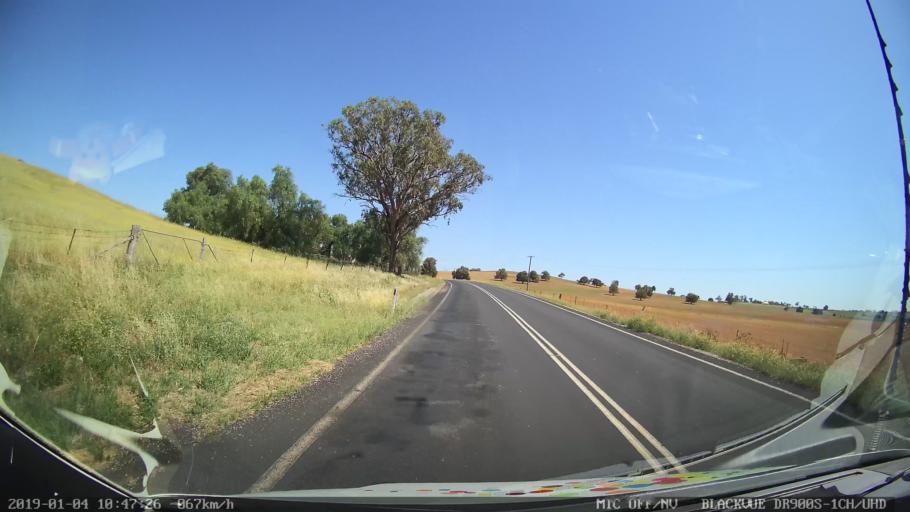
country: AU
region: New South Wales
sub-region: Cabonne
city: Molong
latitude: -33.2699
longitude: 148.7196
